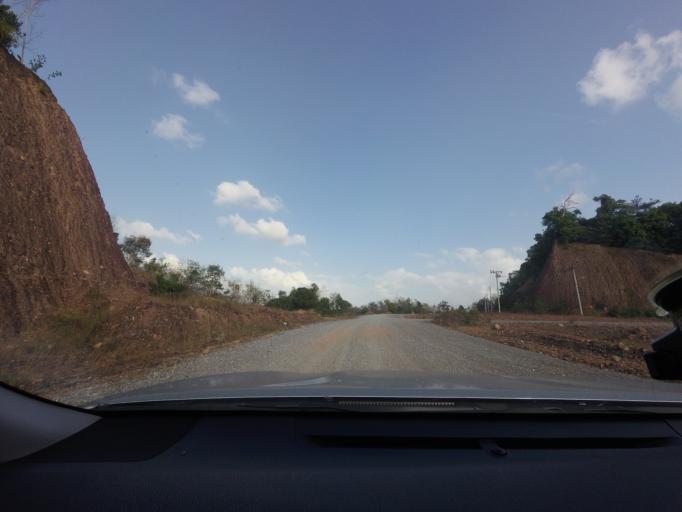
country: TH
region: Pattani
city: Mae Lan
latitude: 6.6065
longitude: 101.2421
